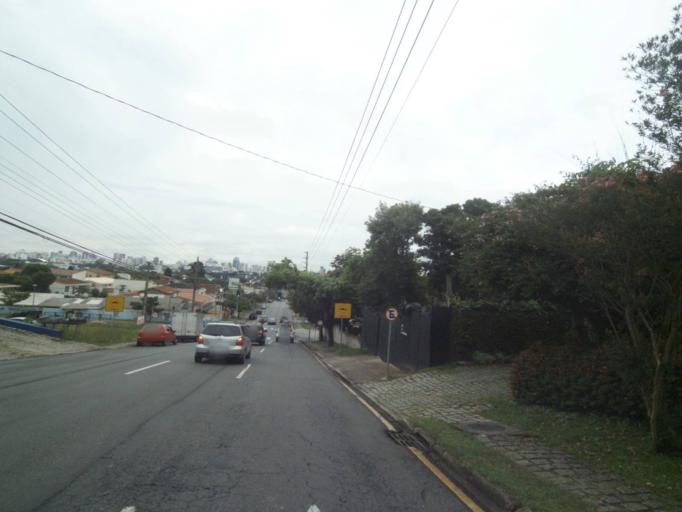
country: BR
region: Parana
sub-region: Curitiba
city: Curitiba
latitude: -25.4150
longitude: -49.2863
